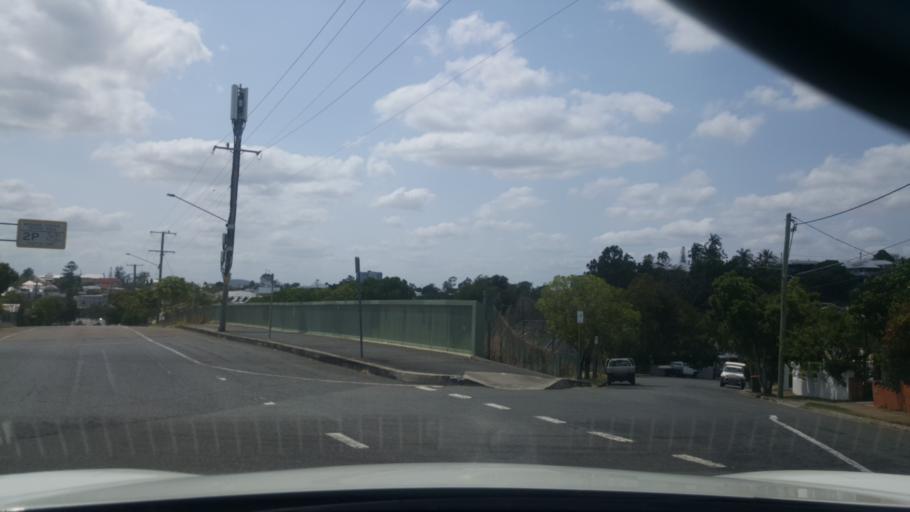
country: AU
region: Queensland
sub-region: Brisbane
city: South Brisbane
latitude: -27.4884
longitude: 153.0238
